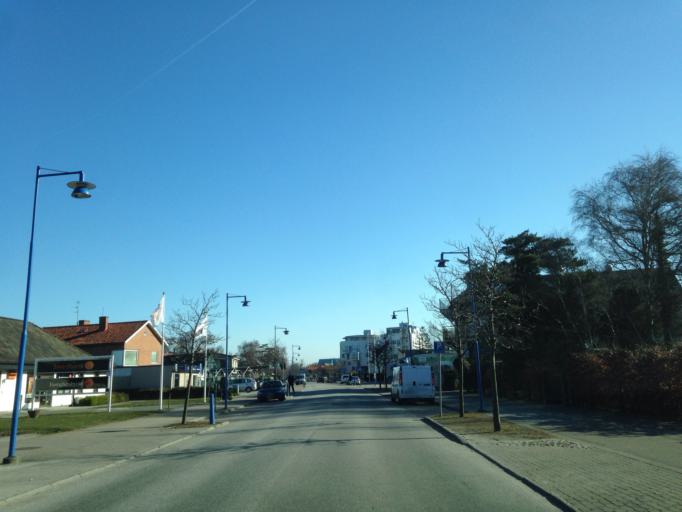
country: SE
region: Skane
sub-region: Vellinge Kommun
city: Hollviken
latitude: 55.4168
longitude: 12.9505
